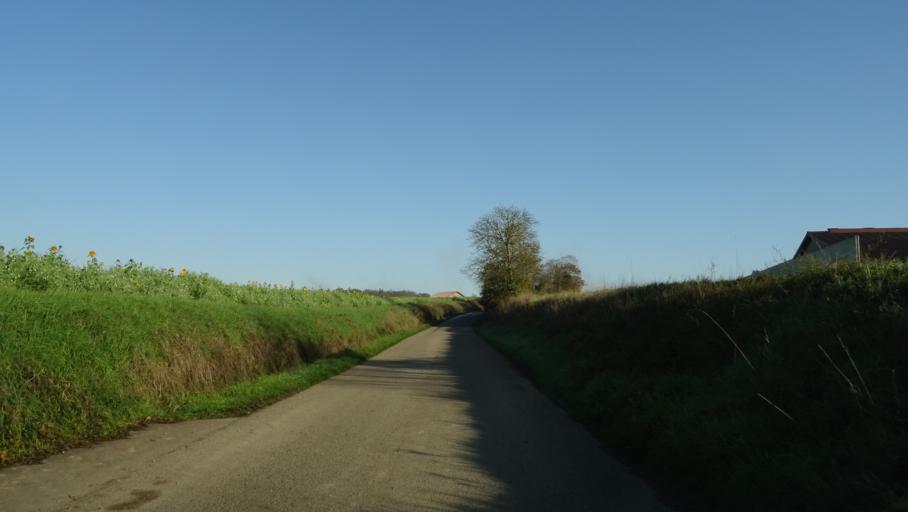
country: DE
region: Baden-Wuerttemberg
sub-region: Karlsruhe Region
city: Binau
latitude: 49.3696
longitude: 9.0682
